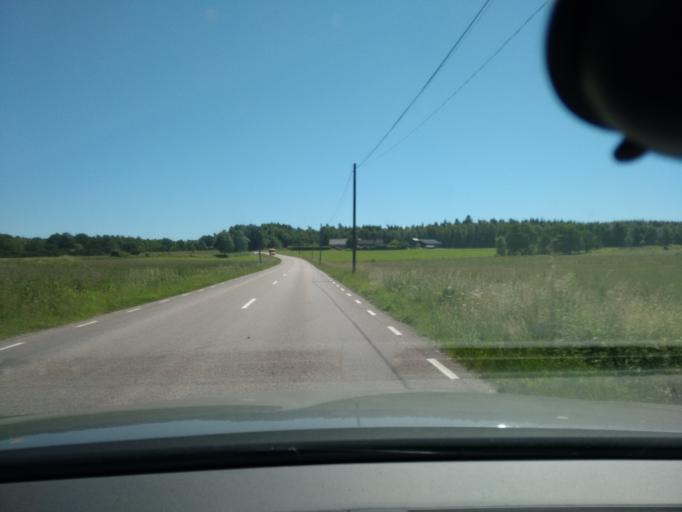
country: SE
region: Skane
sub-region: Horby Kommun
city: Hoerby
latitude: 55.7970
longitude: 13.8074
